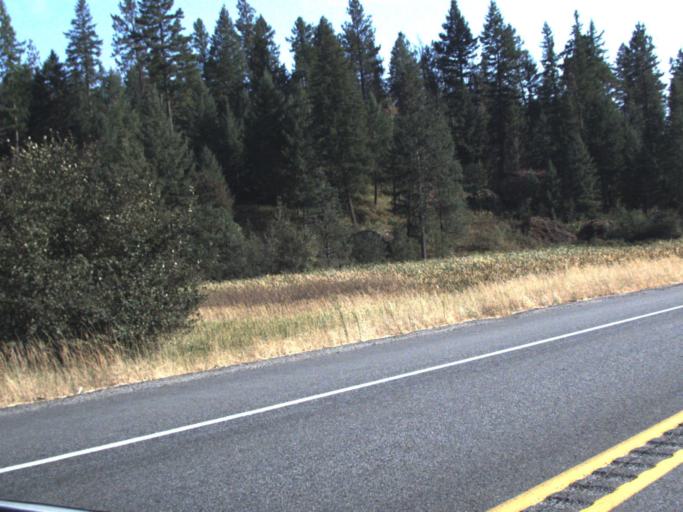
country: US
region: Washington
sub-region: Spokane County
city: Deer Park
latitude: 47.9410
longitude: -117.3506
